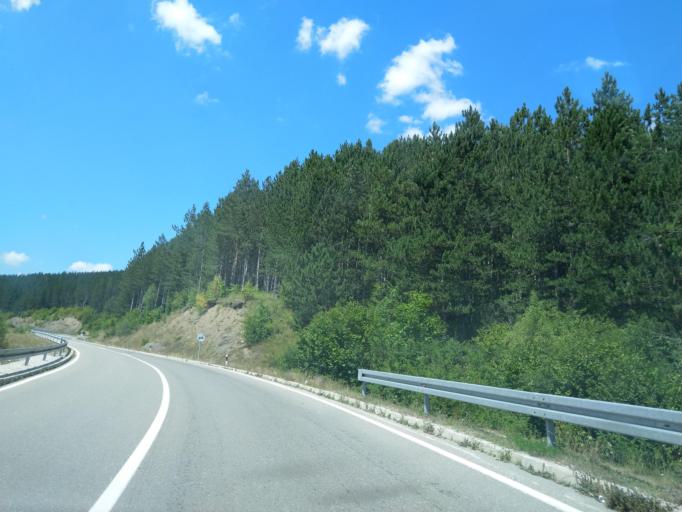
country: RS
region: Central Serbia
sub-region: Zlatiborski Okrug
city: Sjenica
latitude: 43.2993
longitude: 19.9363
